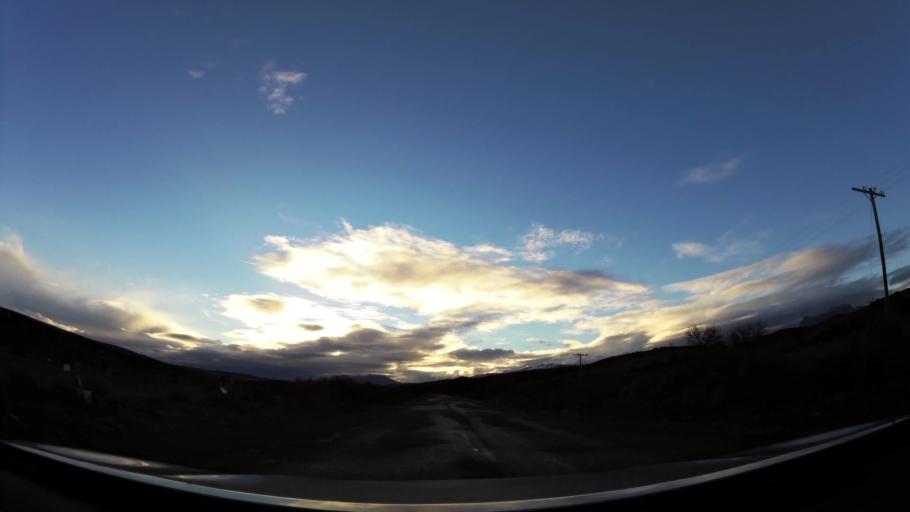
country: ZA
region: Western Cape
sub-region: Eden District Municipality
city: Riversdale
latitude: -34.0699
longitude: 20.9020
